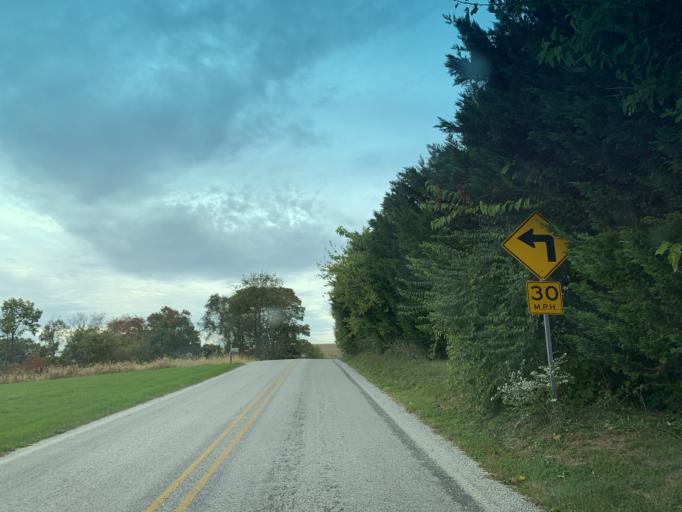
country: US
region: Pennsylvania
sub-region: York County
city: Stewartstown
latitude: 39.8095
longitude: -76.4888
